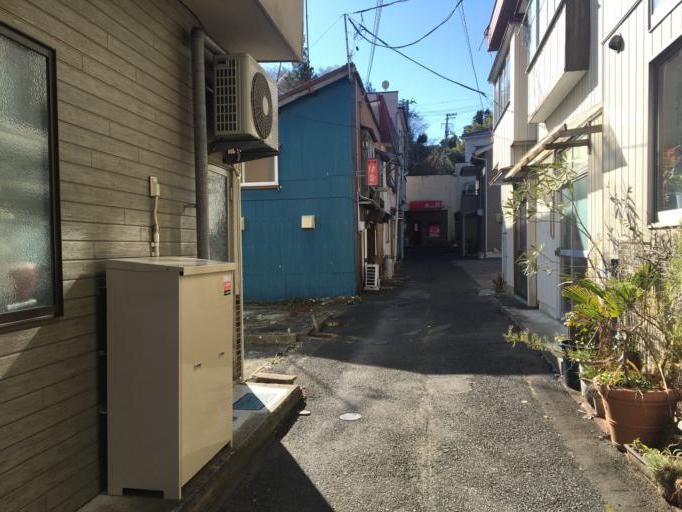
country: JP
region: Iwate
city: Ofunato
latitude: 38.9088
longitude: 141.5595
